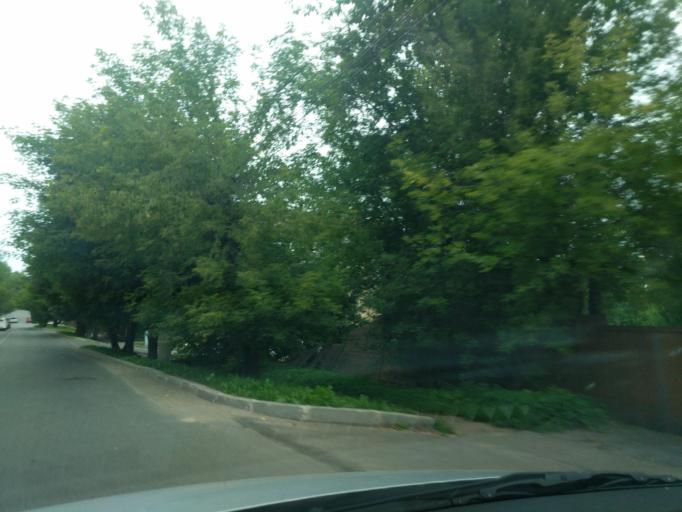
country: RU
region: Kirov
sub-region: Kirovo-Chepetskiy Rayon
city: Kirov
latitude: 58.5985
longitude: 49.6727
